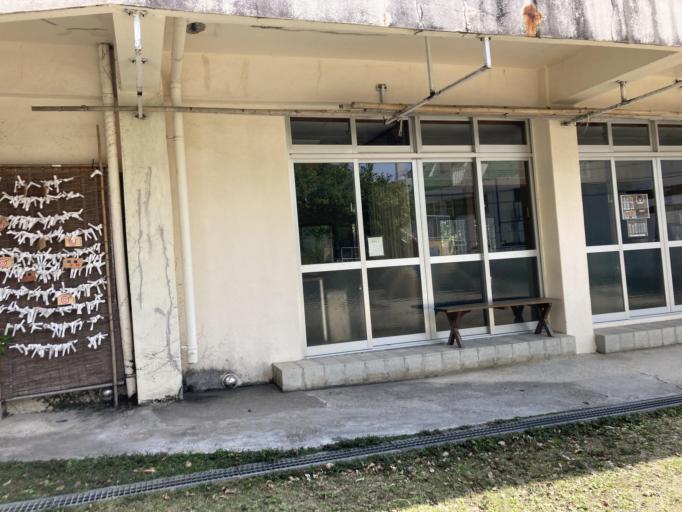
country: JP
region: Okinawa
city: Naha-shi
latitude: 26.2211
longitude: 127.6949
